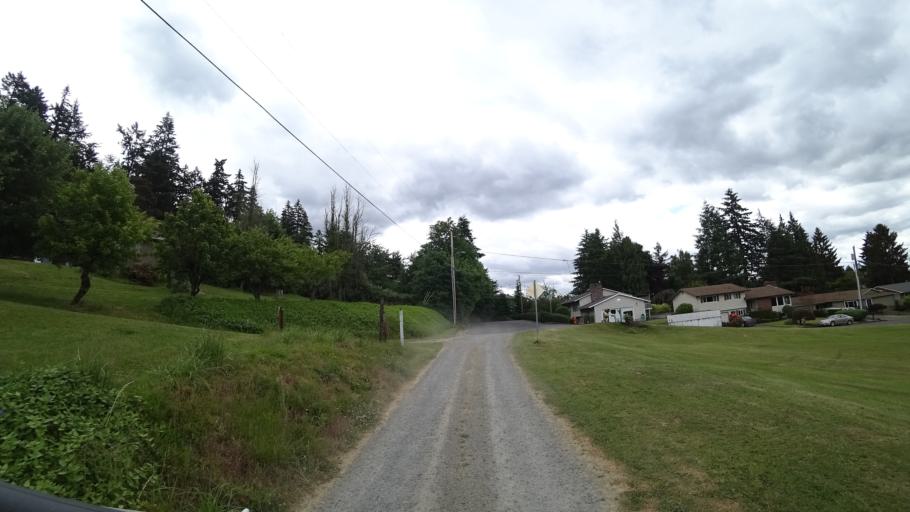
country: US
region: Oregon
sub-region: Clackamas County
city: Happy Valley
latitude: 45.4878
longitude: -122.5193
